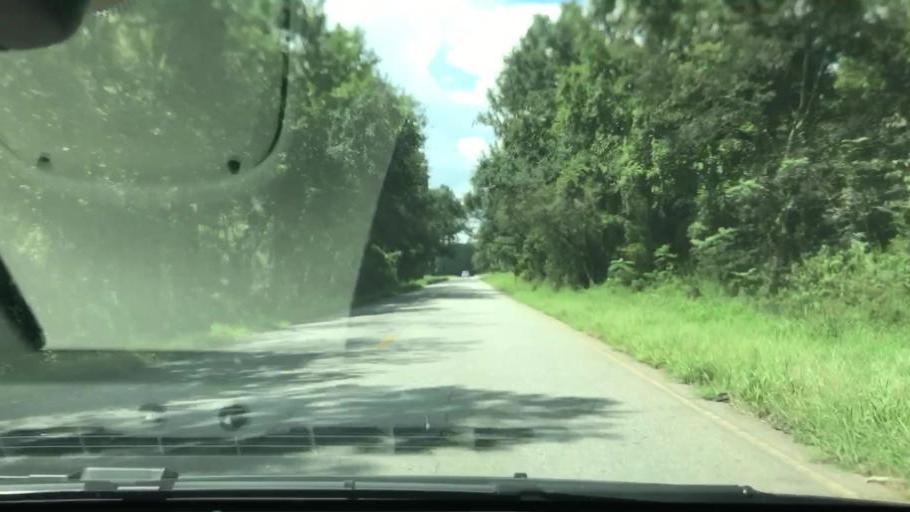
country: US
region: Georgia
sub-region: Seminole County
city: Donalsonville
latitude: 30.9876
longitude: -84.9777
